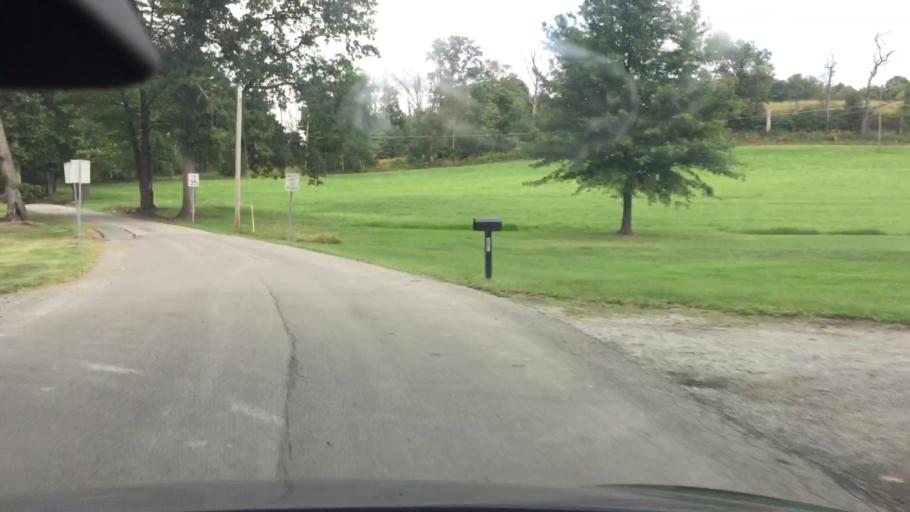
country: US
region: Pennsylvania
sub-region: Butler County
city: Nixon
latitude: 40.7437
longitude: -79.8847
